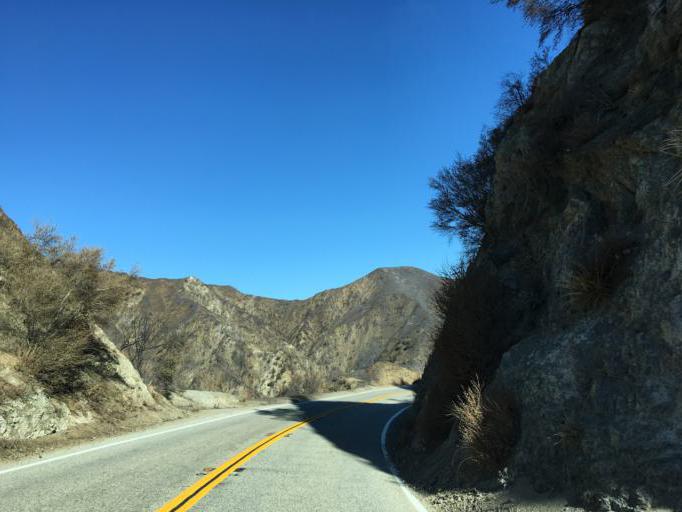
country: US
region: California
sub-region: Los Angeles County
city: San Fernando
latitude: 34.3671
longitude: -118.3963
